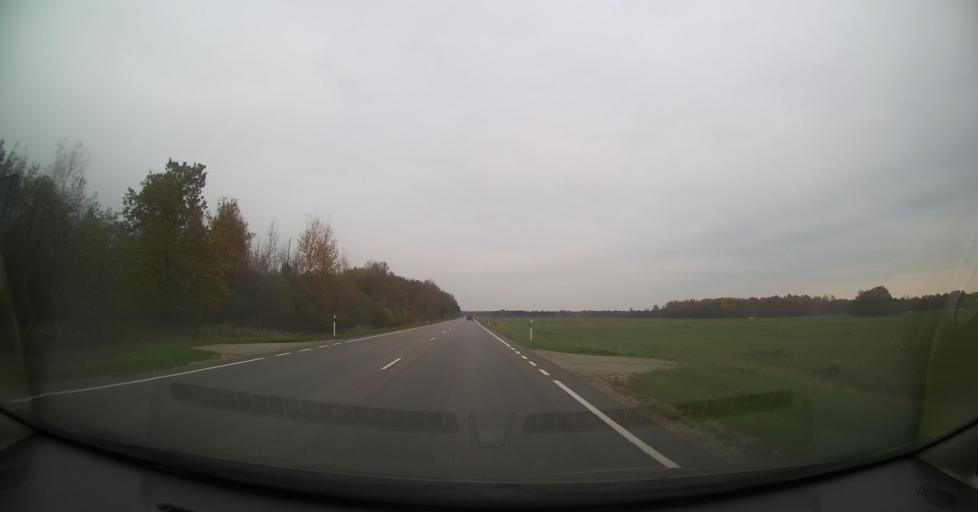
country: EE
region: Laeaene
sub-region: Ridala Parish
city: Uuemoisa
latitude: 58.9688
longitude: 23.8294
